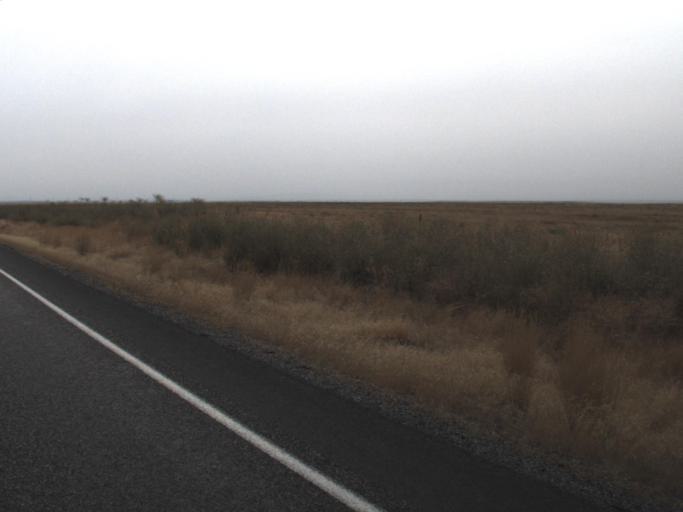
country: US
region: Washington
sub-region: Benton County
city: Benton City
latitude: 46.1622
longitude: -119.6009
